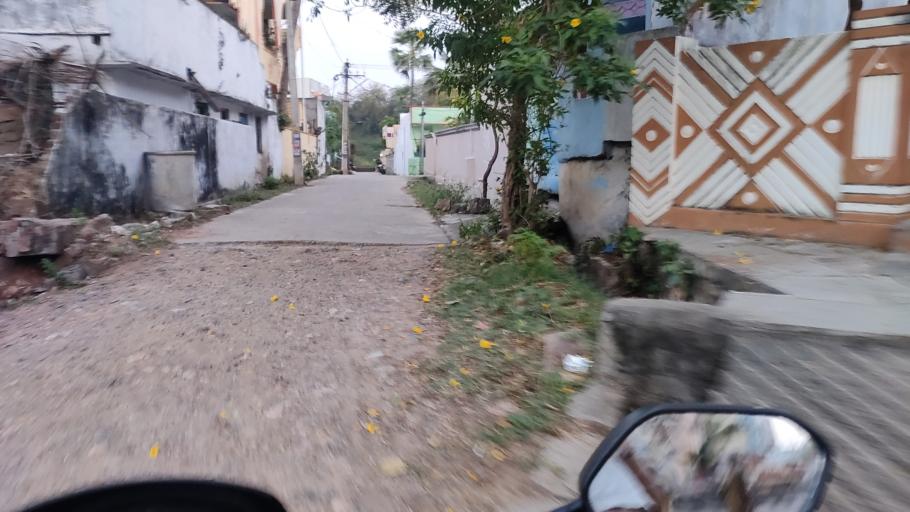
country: IN
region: Telangana
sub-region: Warangal
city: Warangal
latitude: 17.9607
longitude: 79.6024
